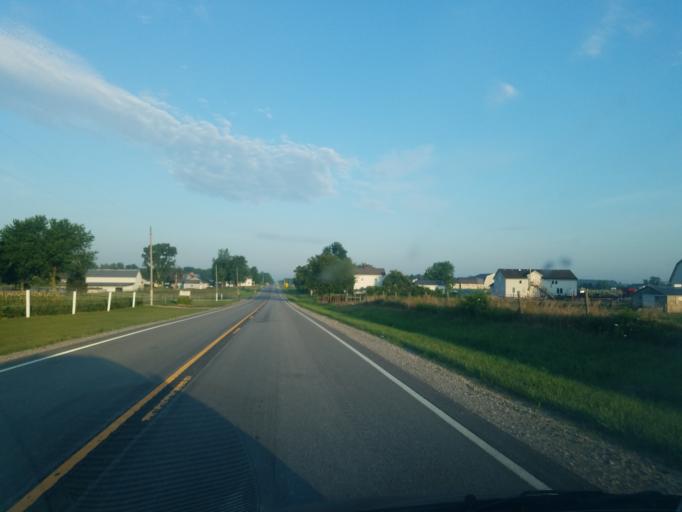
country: US
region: Indiana
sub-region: Allen County
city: Woodburn
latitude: 41.1841
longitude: -84.8564
